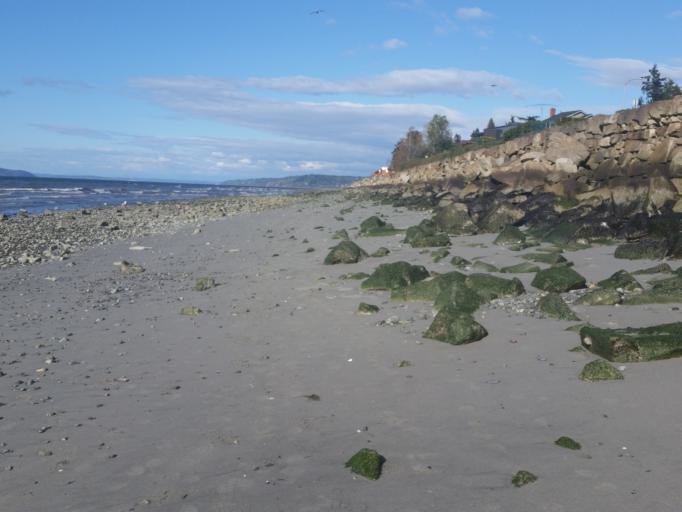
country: US
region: Washington
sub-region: Snohomish County
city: Edmonds
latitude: 47.8171
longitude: -122.3781
